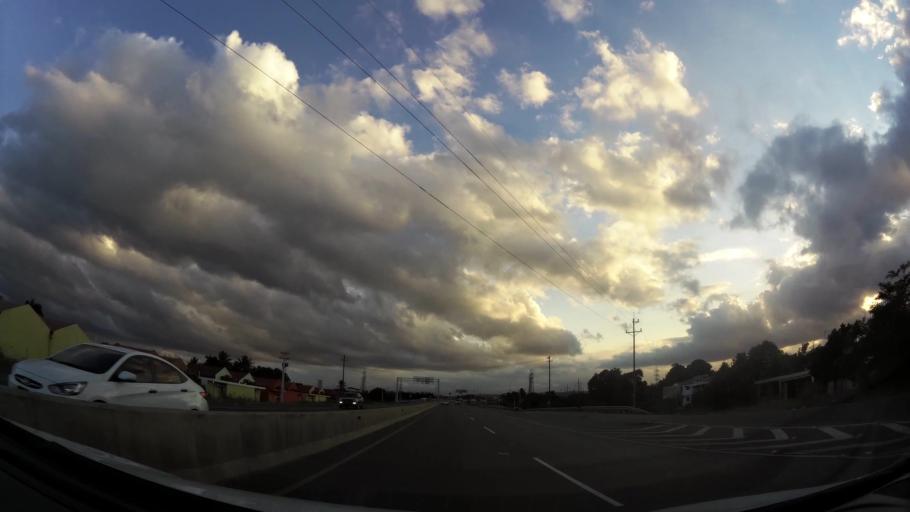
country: DO
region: Santiago
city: Licey al Medio
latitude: 19.4187
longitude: -70.6403
